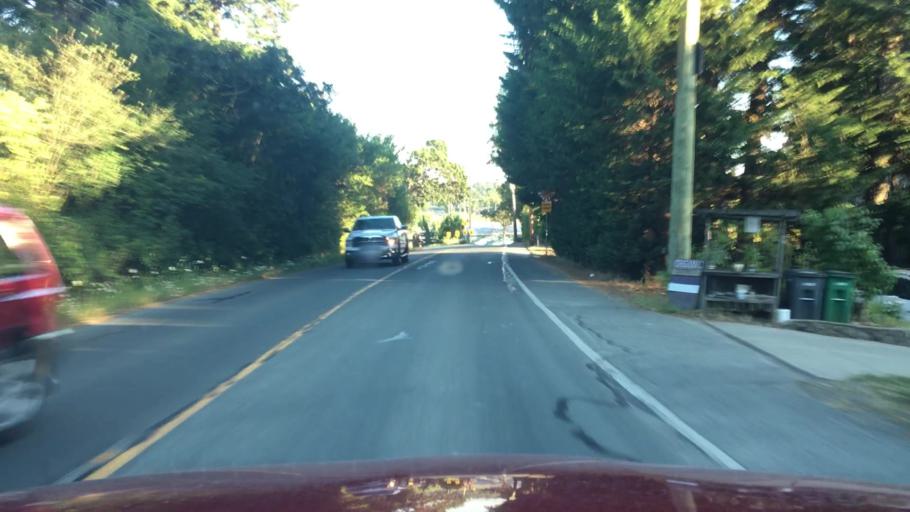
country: CA
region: British Columbia
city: Victoria
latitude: 48.4793
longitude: -123.3544
